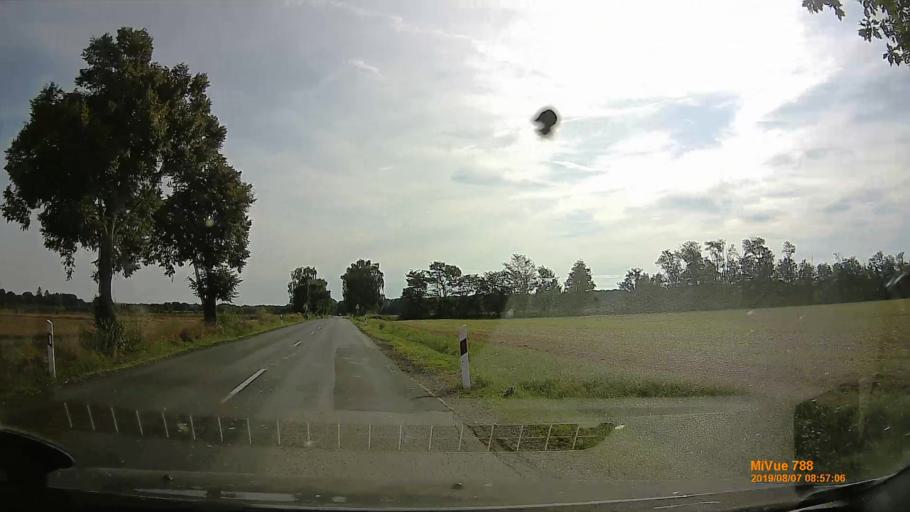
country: HU
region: Zala
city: Pacsa
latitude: 46.7369
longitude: 16.9022
